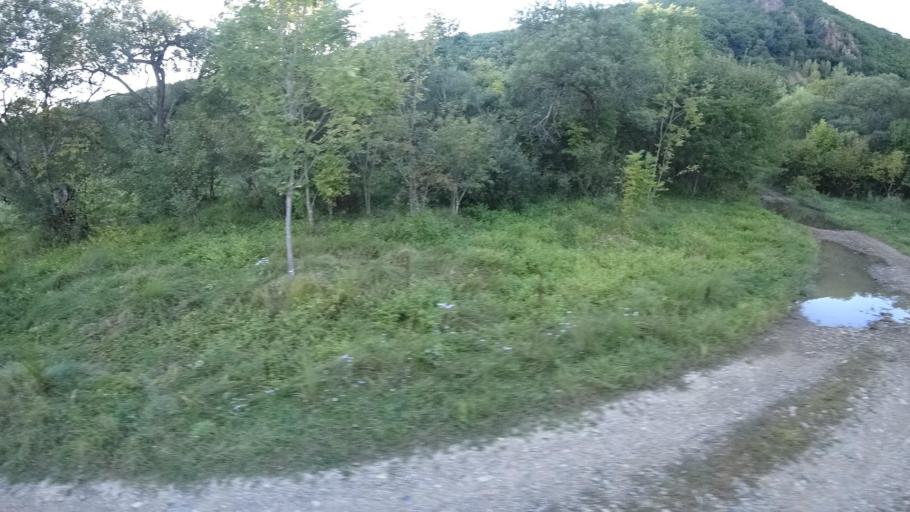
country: RU
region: Primorskiy
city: Kirovskiy
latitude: 44.8350
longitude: 133.5734
